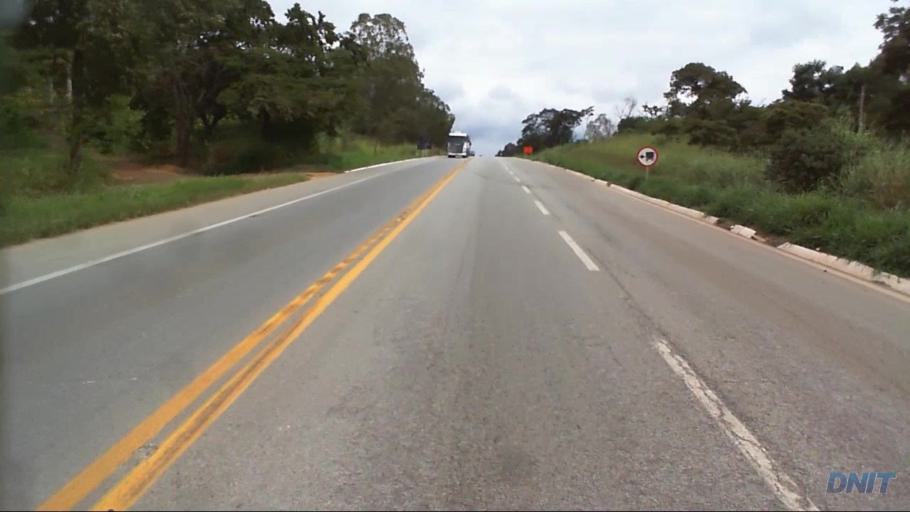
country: BR
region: Minas Gerais
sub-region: Caete
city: Caete
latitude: -19.7696
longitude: -43.6476
